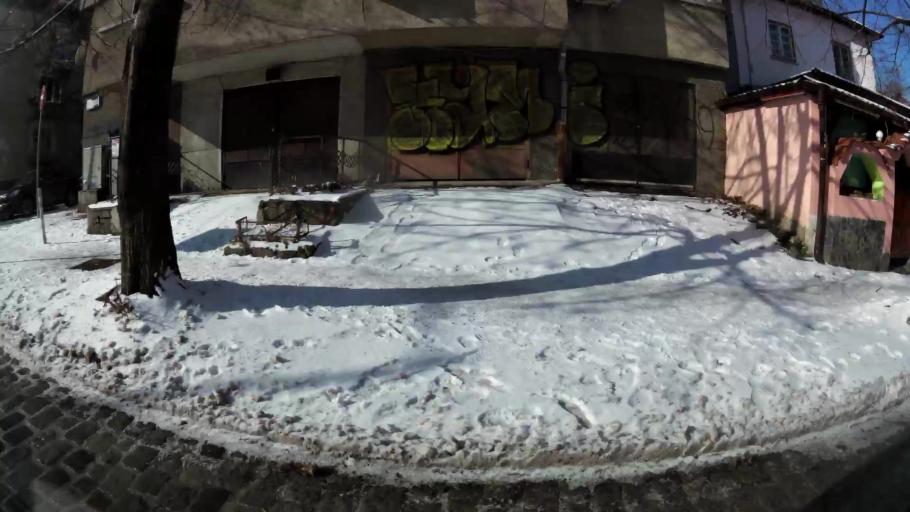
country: BG
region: Sofia-Capital
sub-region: Stolichna Obshtina
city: Sofia
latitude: 42.6795
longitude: 23.3275
